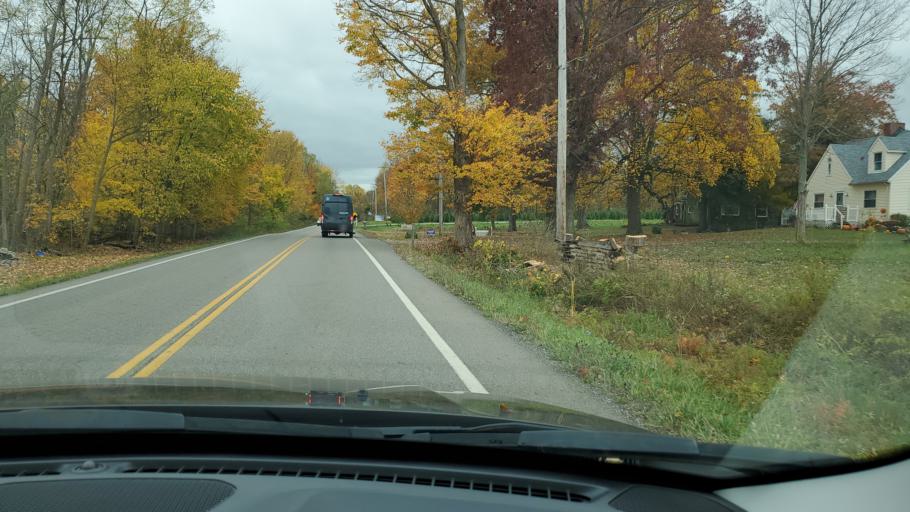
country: US
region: Ohio
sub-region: Mahoning County
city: Boardman
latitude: 40.9538
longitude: -80.6417
